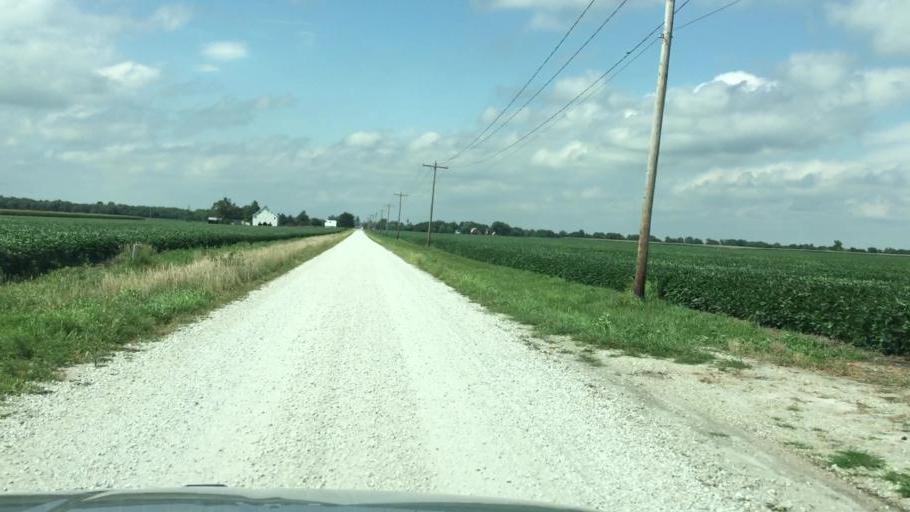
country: US
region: Illinois
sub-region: Hancock County
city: Carthage
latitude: 40.5283
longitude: -91.1576
